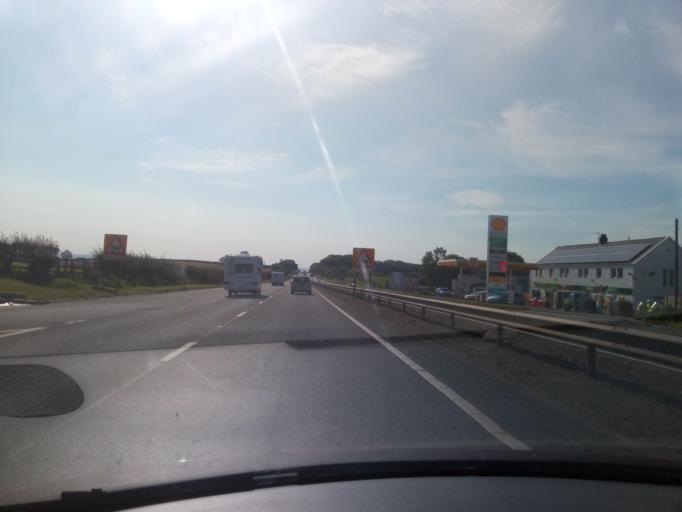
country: GB
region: England
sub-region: Hartlepool
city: Elwick
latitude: 54.6543
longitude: -1.3029
